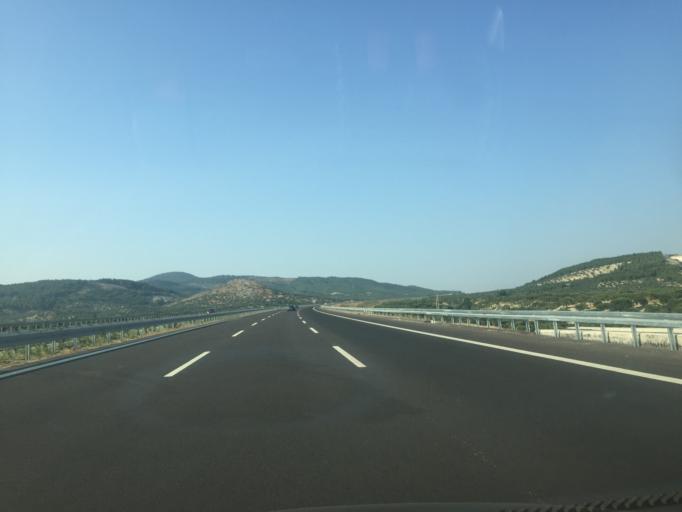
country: TR
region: Manisa
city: Zeytinliova
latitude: 38.9806
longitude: 27.7313
